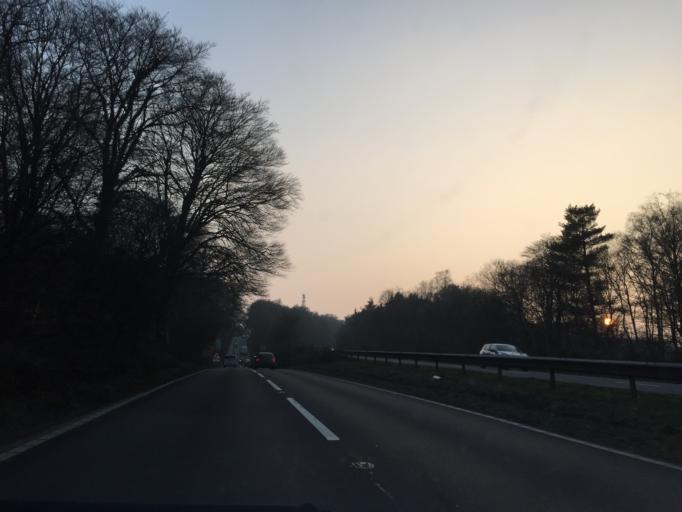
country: GB
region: England
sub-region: Hampshire
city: Cadnam
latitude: 50.9101
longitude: -1.6068
